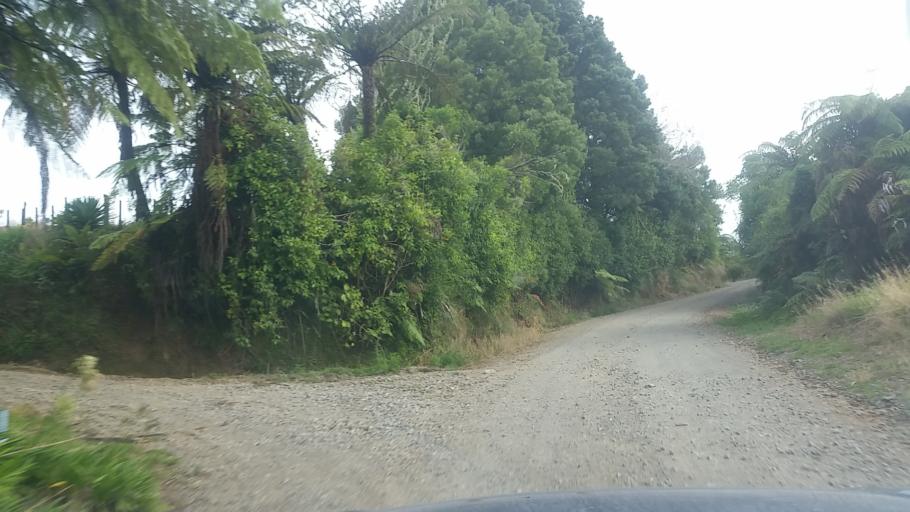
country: NZ
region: Taranaki
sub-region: South Taranaki District
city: Eltham
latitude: -39.1681
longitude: 174.6283
